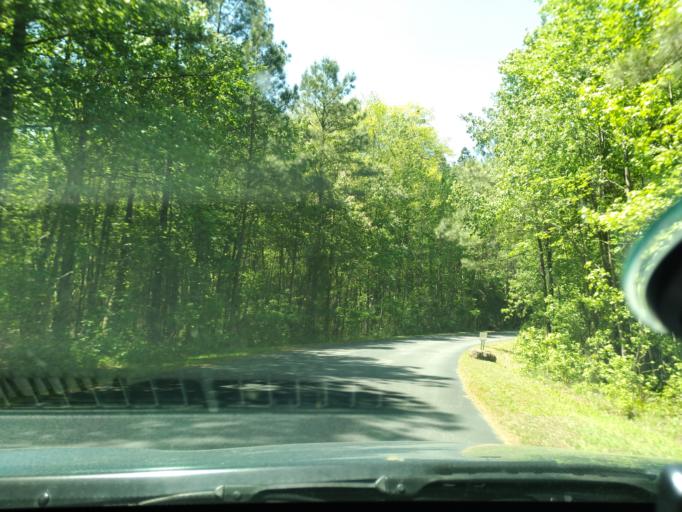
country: US
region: Virginia
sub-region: Prince George County
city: Prince George
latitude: 37.2147
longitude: -77.3085
